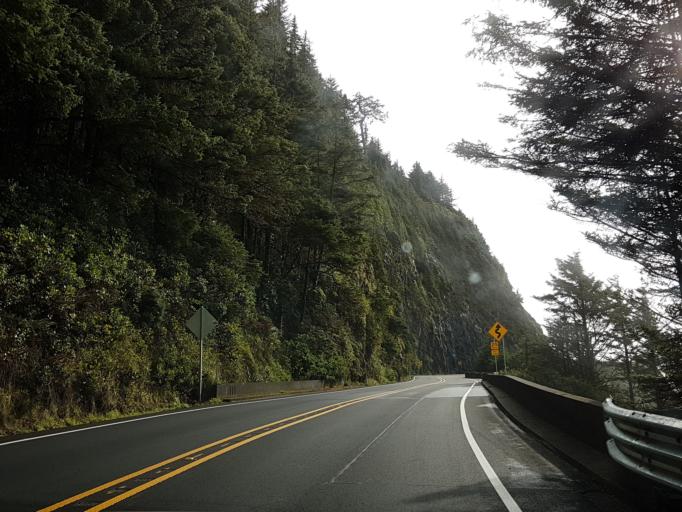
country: US
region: Oregon
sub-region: Lane County
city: Florence
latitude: 44.1271
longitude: -124.1236
